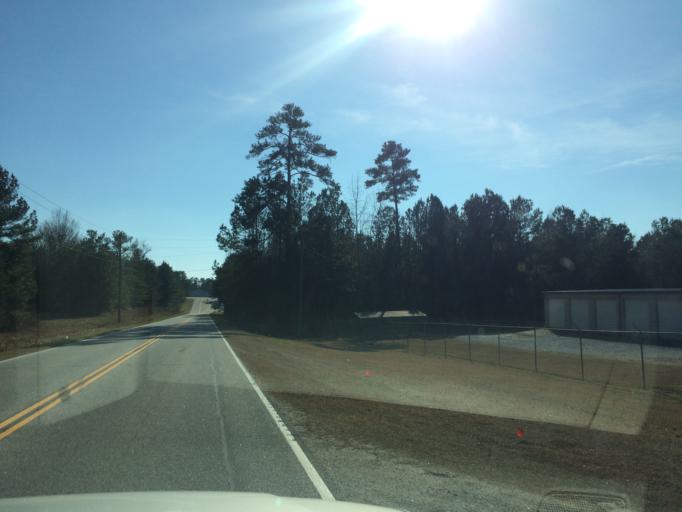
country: US
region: South Carolina
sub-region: Greenwood County
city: Ninety Six
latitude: 34.2920
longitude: -82.0464
